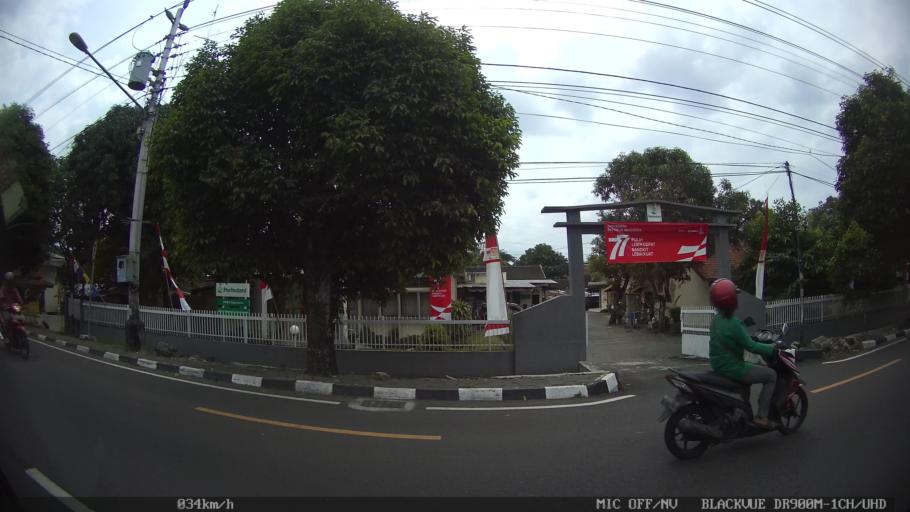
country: ID
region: Daerah Istimewa Yogyakarta
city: Yogyakarta
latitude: -7.7903
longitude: 110.3812
